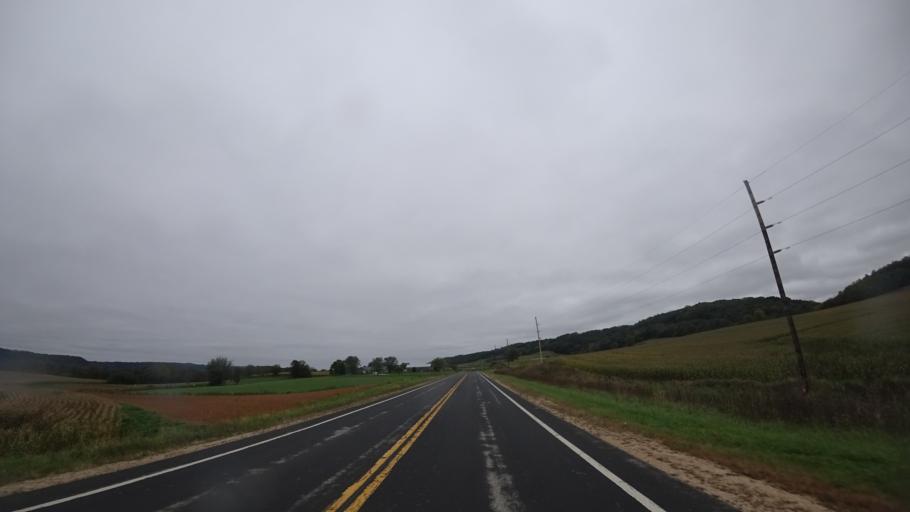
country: US
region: Wisconsin
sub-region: Grant County
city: Boscobel
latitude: 43.1049
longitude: -90.8151
